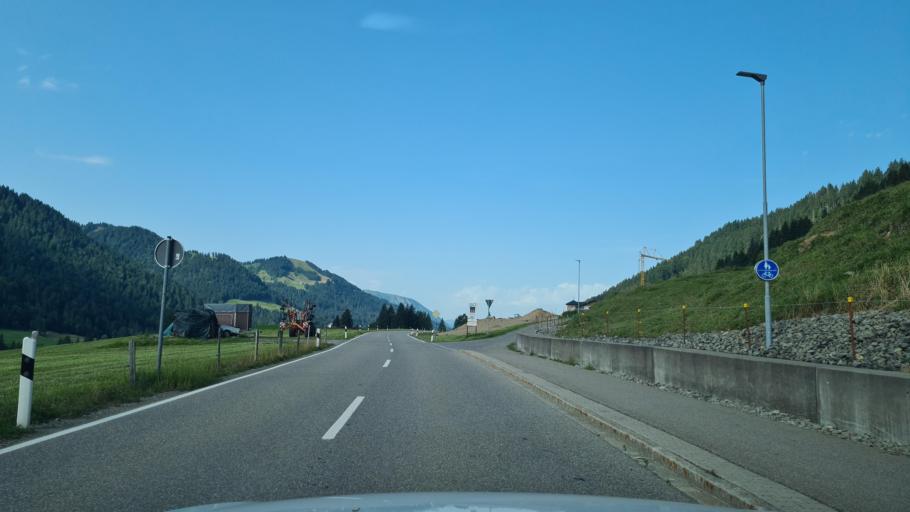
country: DE
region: Bavaria
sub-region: Swabia
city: Balderschwang
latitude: 47.4622
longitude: 10.0845
